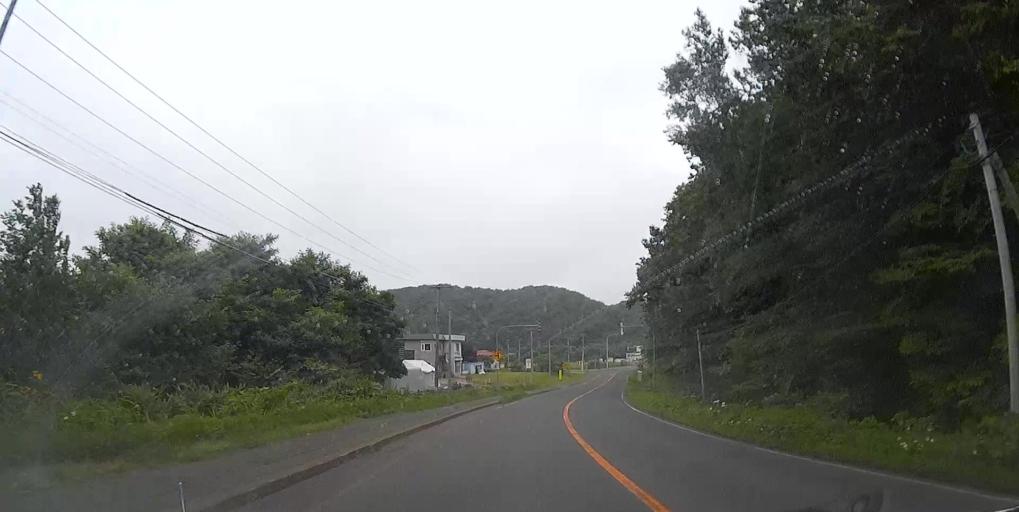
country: JP
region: Hokkaido
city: Iwanai
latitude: 42.4348
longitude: 139.9978
